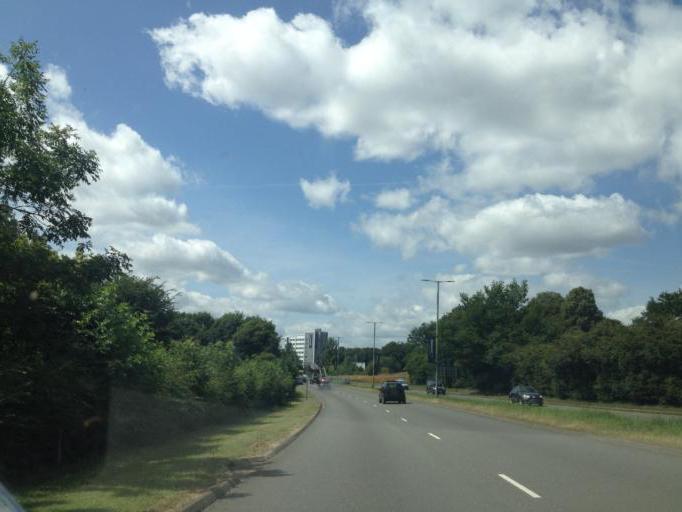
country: GB
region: England
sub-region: Hertfordshire
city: Hemel Hempstead
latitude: 51.7556
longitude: -0.4319
